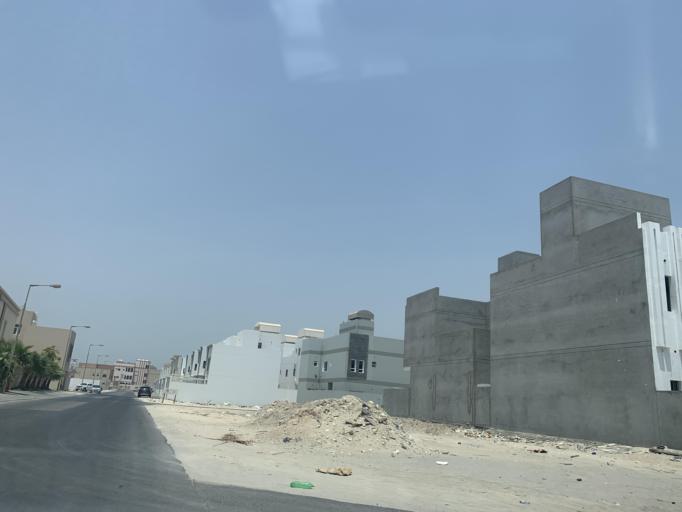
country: BH
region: Manama
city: Jidd Hafs
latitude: 26.2113
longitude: 50.4705
